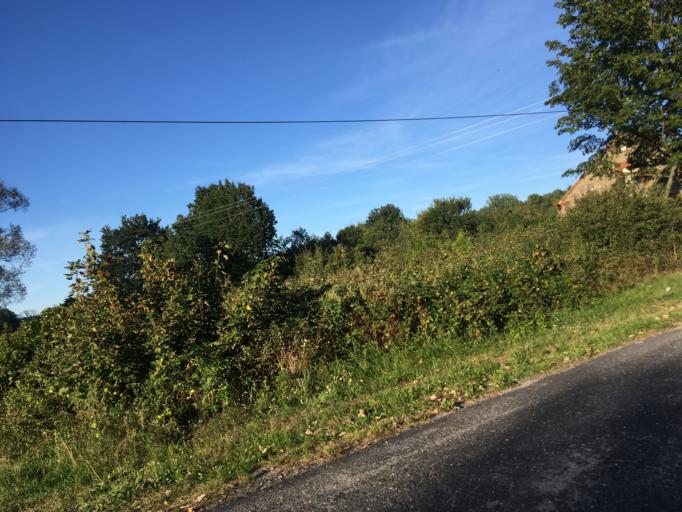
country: PL
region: Lubusz
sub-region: Powiat zarski
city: Trzebiel
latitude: 51.6204
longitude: 14.7653
